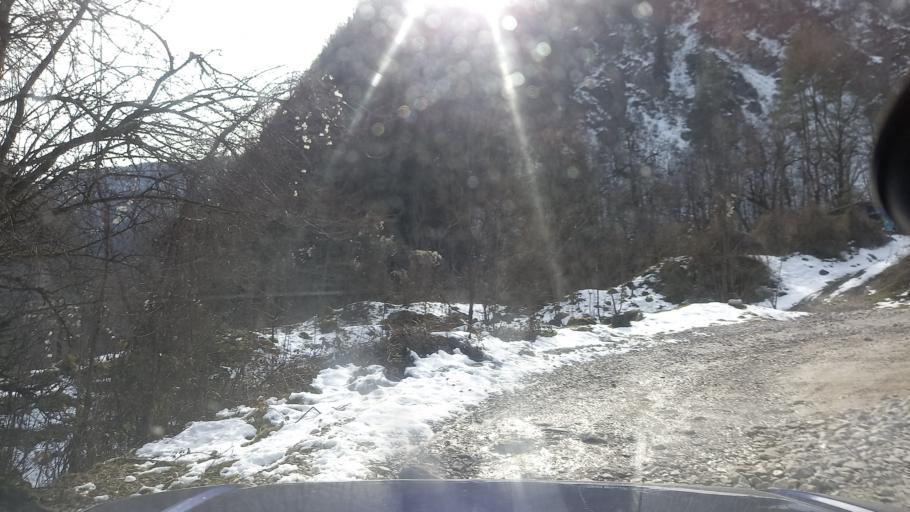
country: GE
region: Abkhazia
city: Gagra
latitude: 43.4099
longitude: 40.4621
